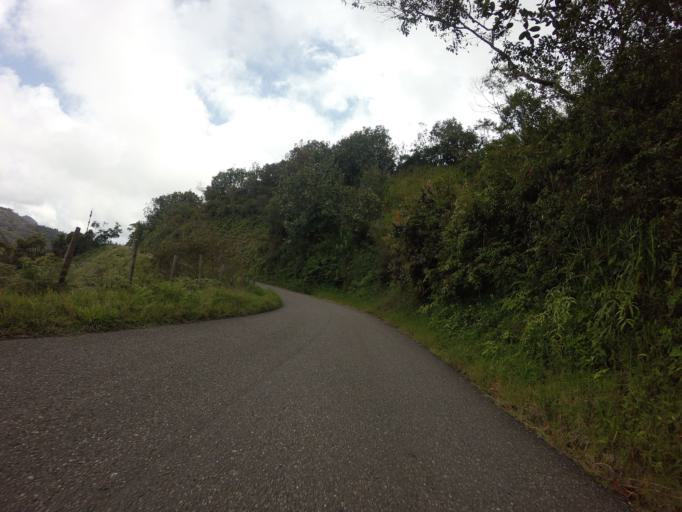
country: CO
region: Caldas
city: Manzanares
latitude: 5.2694
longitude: -75.1319
